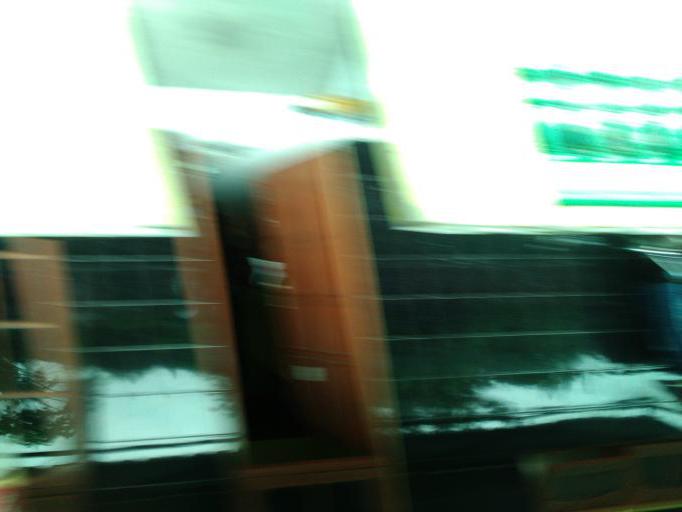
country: ID
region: Central Java
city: Delanggu
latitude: -7.6163
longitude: 110.6994
